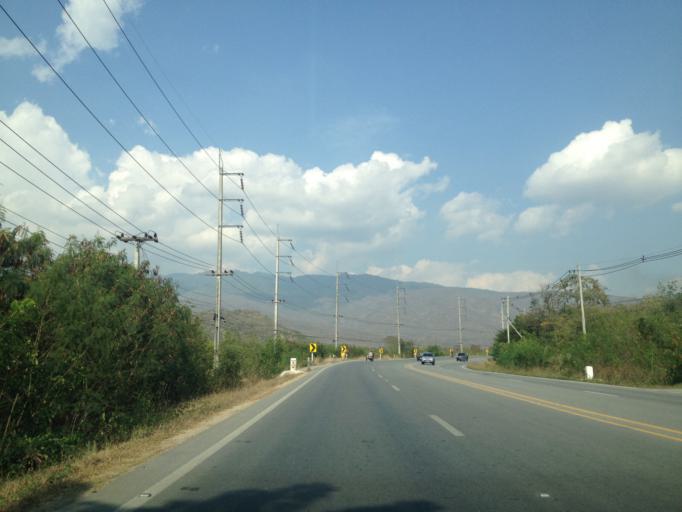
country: TH
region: Chiang Mai
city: Hot
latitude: 18.2995
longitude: 98.6417
